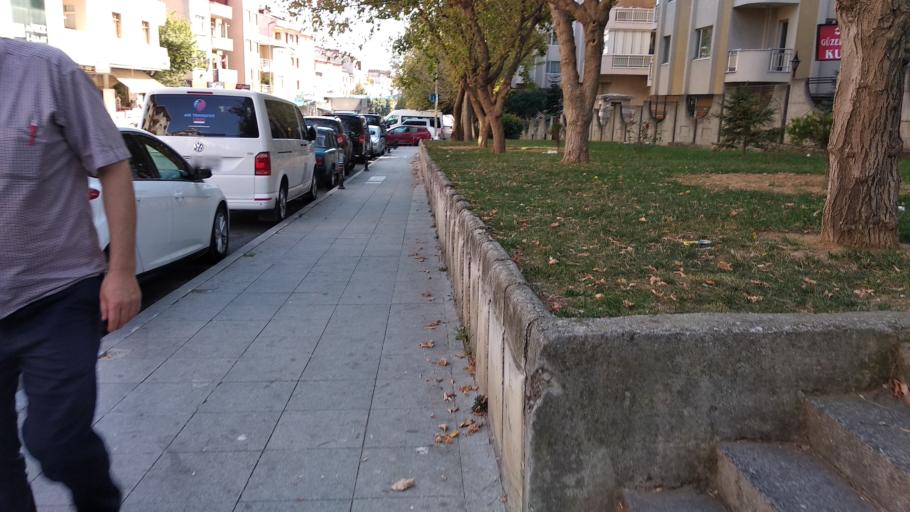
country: TR
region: Istanbul
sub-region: Atasehir
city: Atasehir
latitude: 41.0040
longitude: 29.0735
